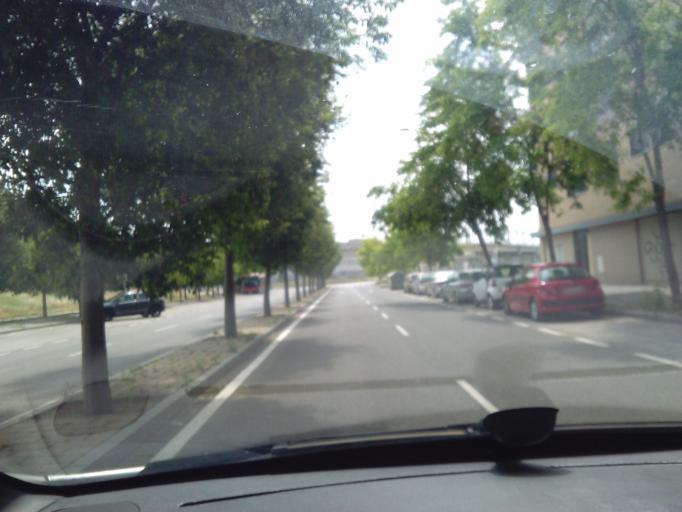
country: ES
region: Andalusia
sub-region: Provincia de Sevilla
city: Sevilla
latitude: 37.3663
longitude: -5.9513
